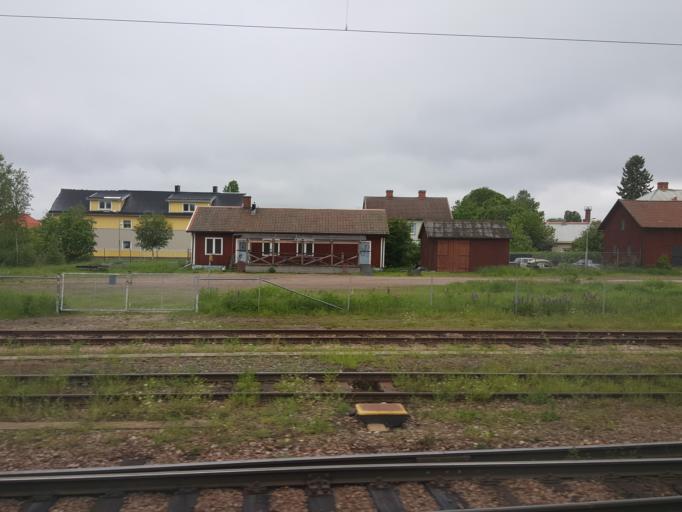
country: SE
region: Dalarna
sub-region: Avesta Kommun
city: Avesta
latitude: 60.1265
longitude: 16.2178
